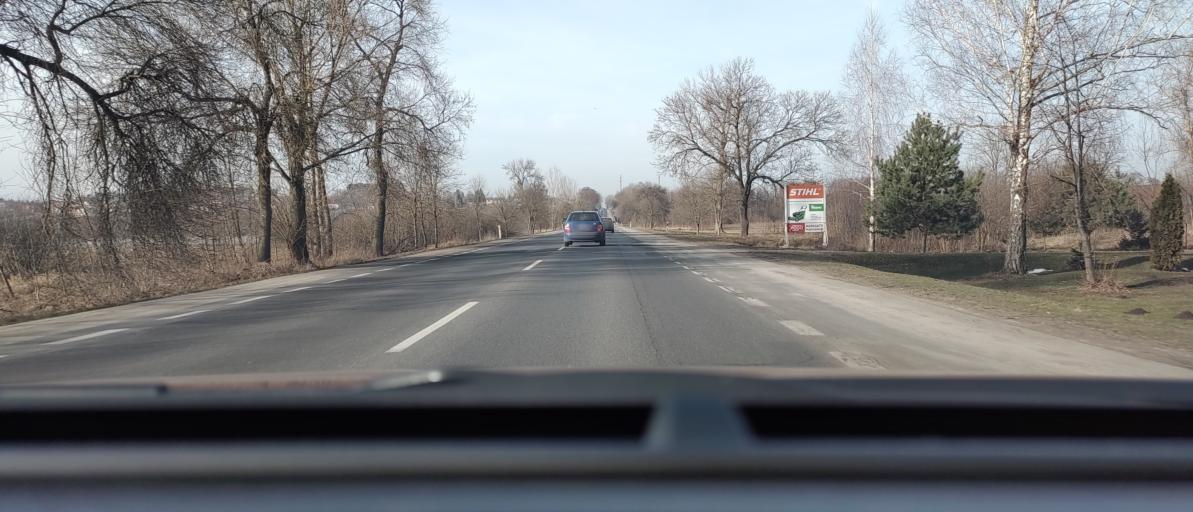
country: PL
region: Masovian Voivodeship
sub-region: Powiat bialobrzeski
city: Promna
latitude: 51.6654
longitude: 20.9483
